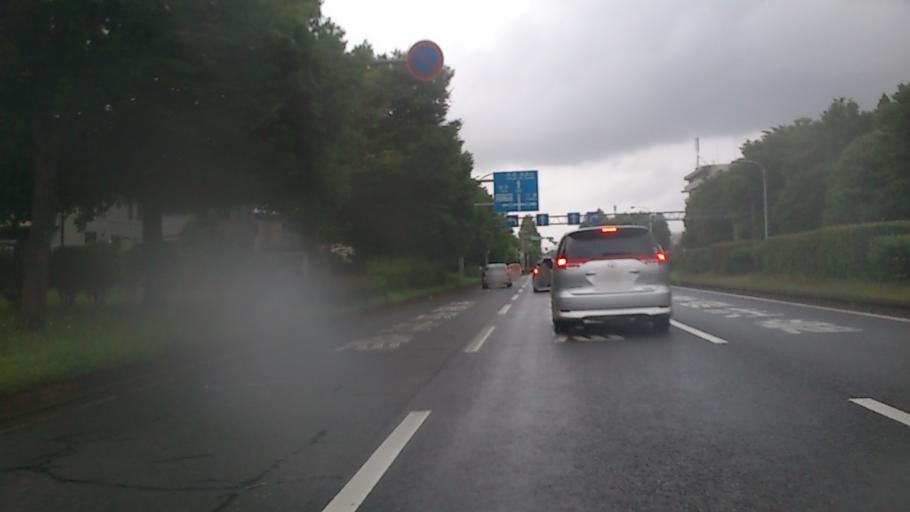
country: JP
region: Ibaraki
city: Naka
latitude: 36.0855
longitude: 140.1043
